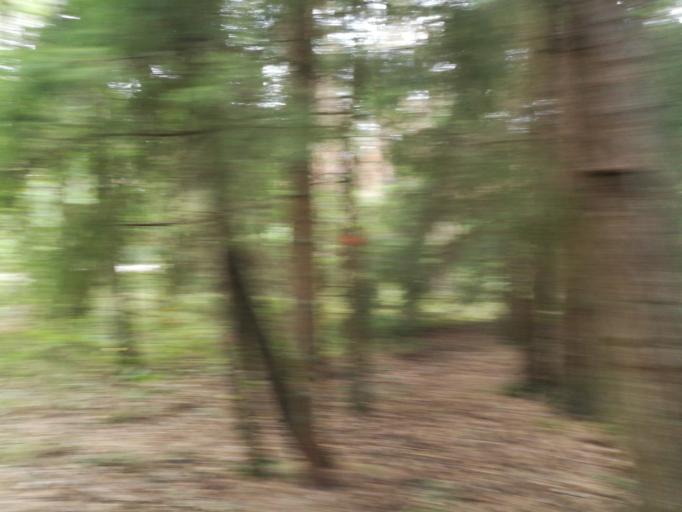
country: DE
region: Bavaria
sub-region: Regierungsbezirk Mittelfranken
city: Seukendorf
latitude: 49.4720
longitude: 10.8917
